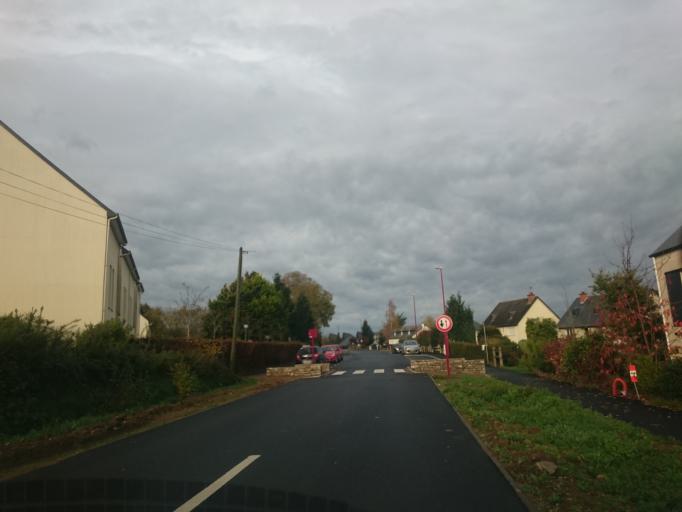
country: FR
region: Brittany
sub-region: Departement d'Ille-et-Vilaine
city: Bourg-des-Comptes
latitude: 47.9280
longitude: -1.7331
